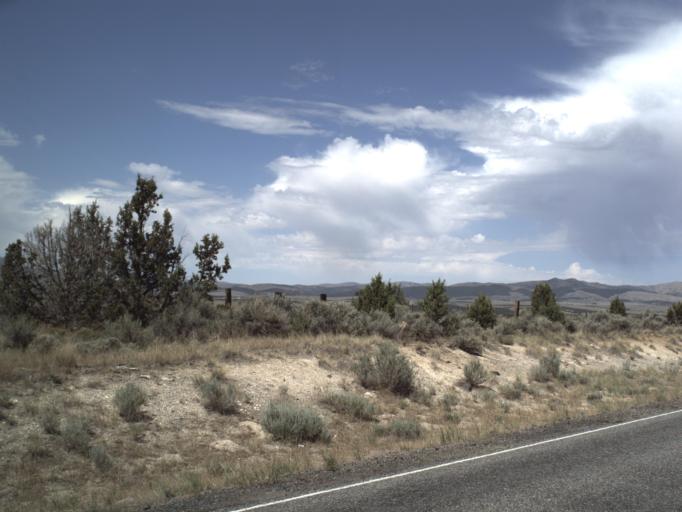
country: US
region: Utah
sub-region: Juab County
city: Mona
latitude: 39.9248
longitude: -112.1557
